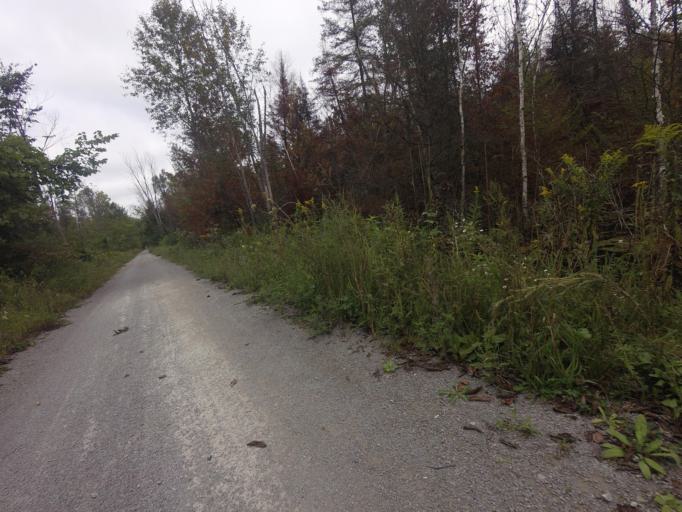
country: CA
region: Ontario
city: Uxbridge
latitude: 44.2539
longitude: -79.0329
